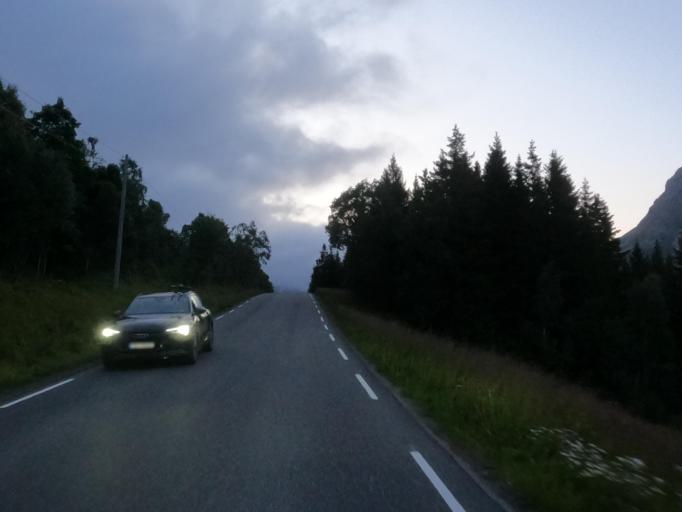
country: NO
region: Nordland
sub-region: Lodingen
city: Lodingen
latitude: 68.5869
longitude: 15.7909
